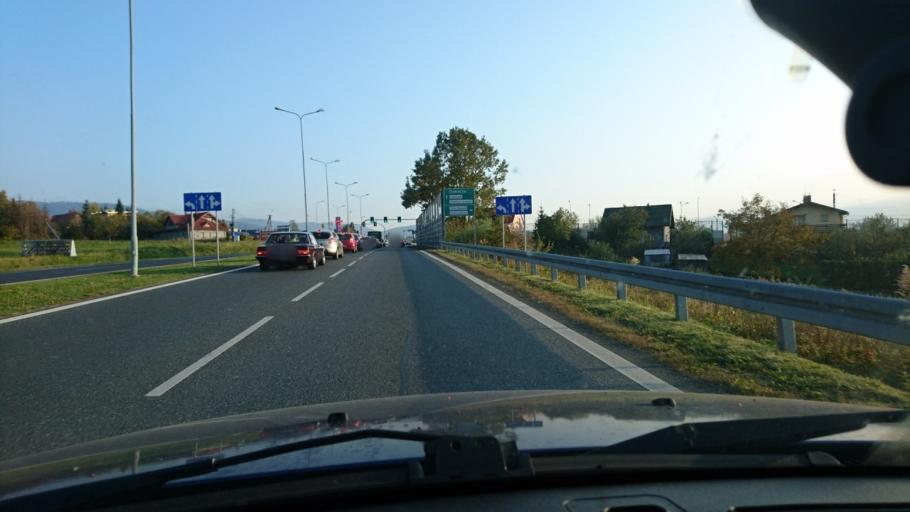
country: PL
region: Silesian Voivodeship
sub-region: Bielsko-Biala
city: Bielsko-Biala
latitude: 49.8403
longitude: 19.0701
